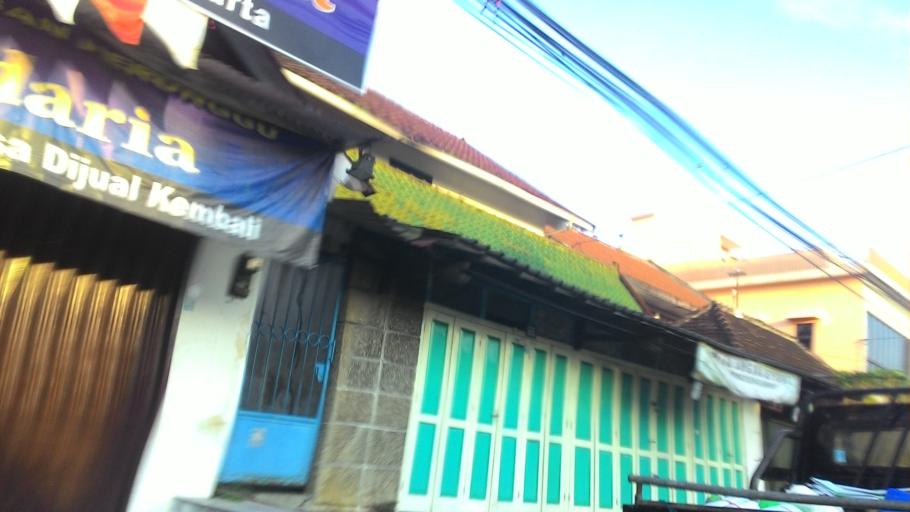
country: ID
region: Daerah Istimewa Yogyakarta
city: Yogyakarta
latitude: -7.7925
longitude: 110.3676
